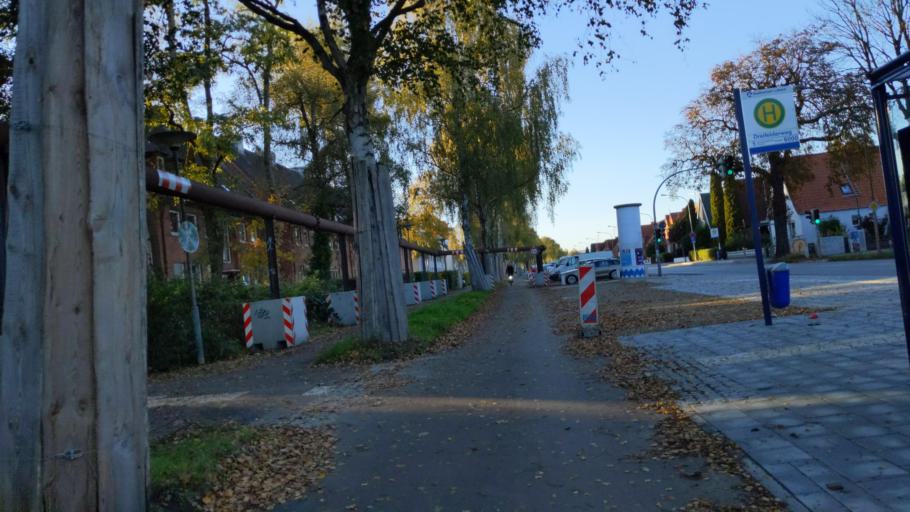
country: DE
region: Schleswig-Holstein
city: Luebeck
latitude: 53.8587
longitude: 10.7319
